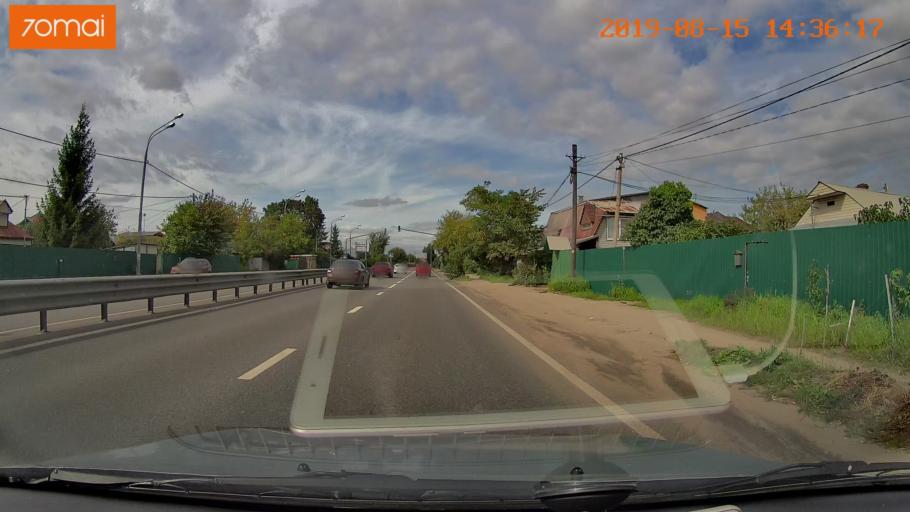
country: RU
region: Moskovskaya
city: Tomilino
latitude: 55.6450
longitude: 37.9356
